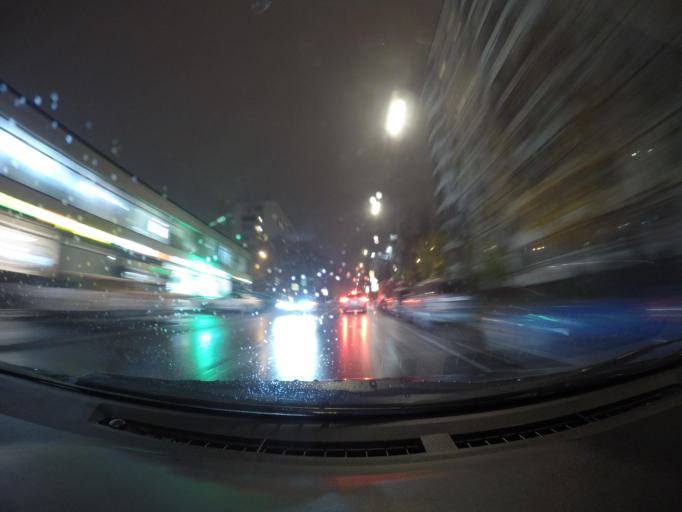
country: RU
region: Moscow
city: Sokol'niki
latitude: 55.7871
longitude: 37.6755
